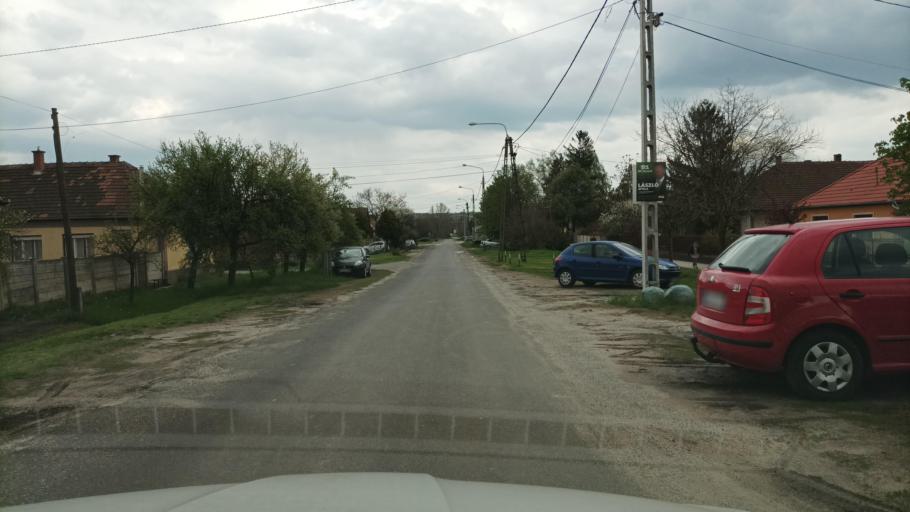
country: HU
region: Pest
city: Cegledbercel
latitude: 47.2167
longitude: 19.6577
